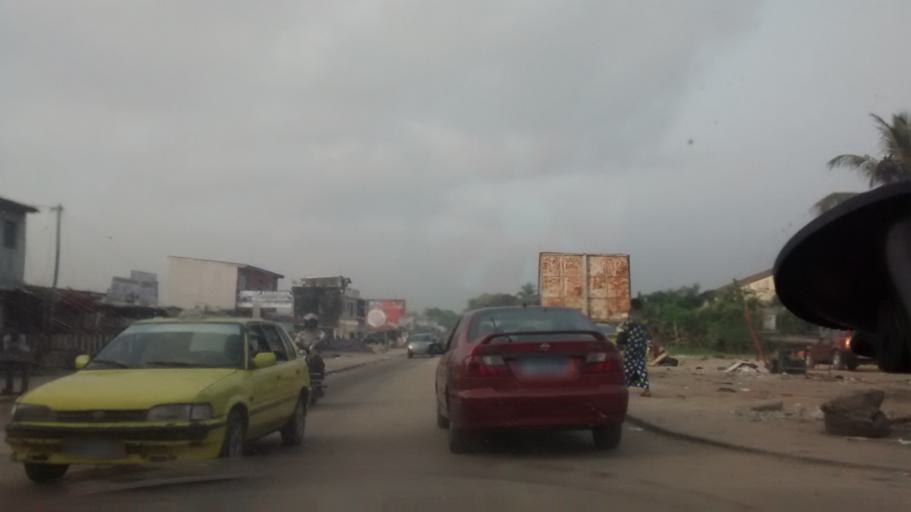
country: CI
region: Lagunes
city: Abobo
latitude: 5.4099
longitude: -3.9853
